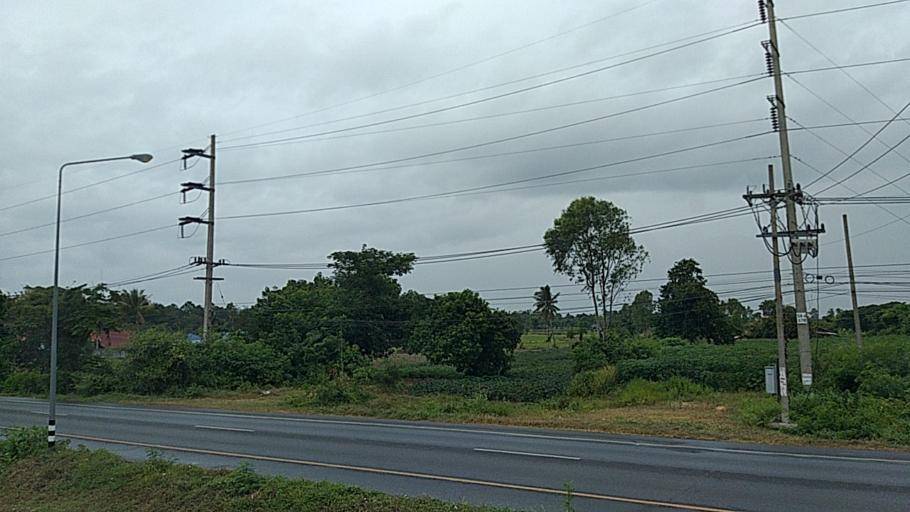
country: TH
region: Maha Sarakham
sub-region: Amphoe Borabue
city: Borabue
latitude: 16.0588
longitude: 103.1366
